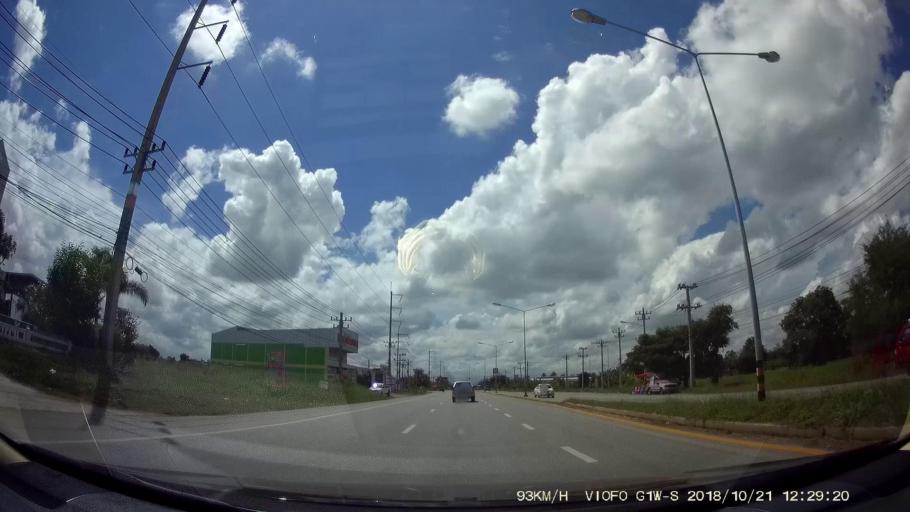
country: TH
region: Nakhon Ratchasima
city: Dan Khun Thot
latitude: 15.1816
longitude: 101.7516
